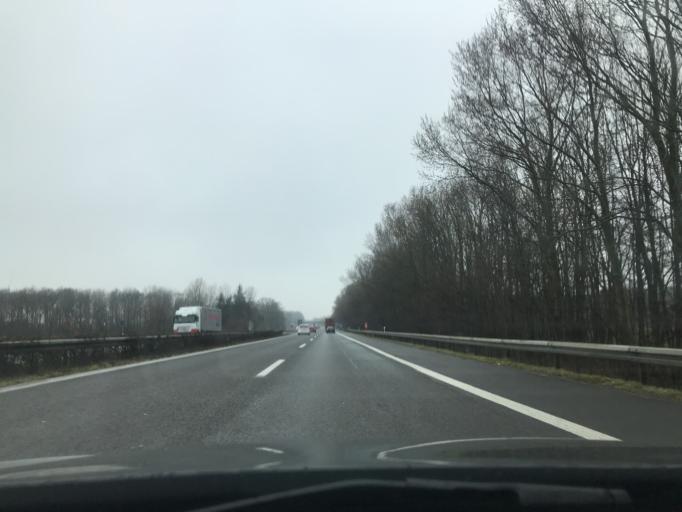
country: DE
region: North Rhine-Westphalia
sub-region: Regierungsbezirk Dusseldorf
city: Sonsbeck
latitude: 51.6070
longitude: 6.3468
